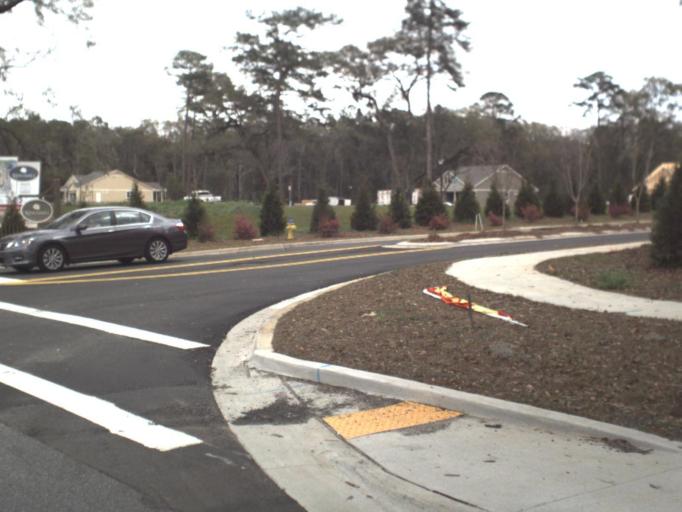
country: US
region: Florida
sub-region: Leon County
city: Tallahassee
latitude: 30.5491
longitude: -84.2245
